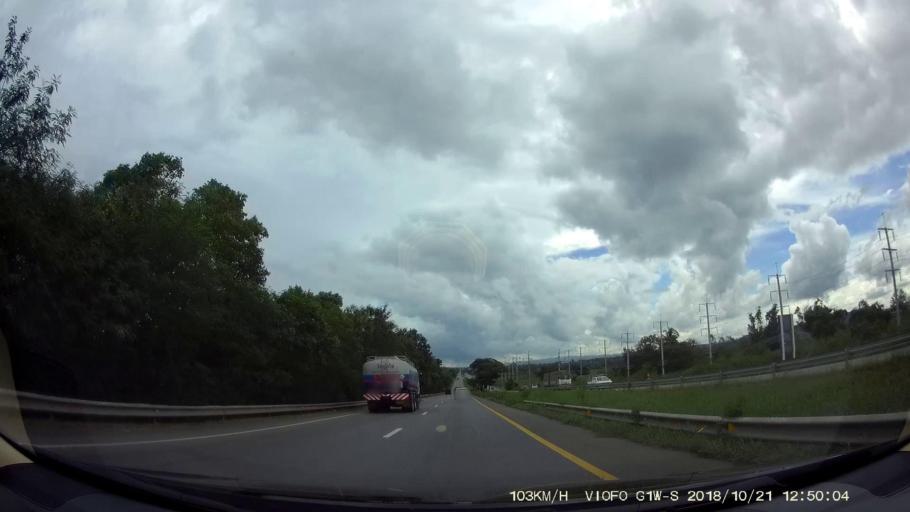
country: TH
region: Nakhon Ratchasima
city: Amphoe Sikhiu
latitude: 14.8877
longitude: 101.6878
